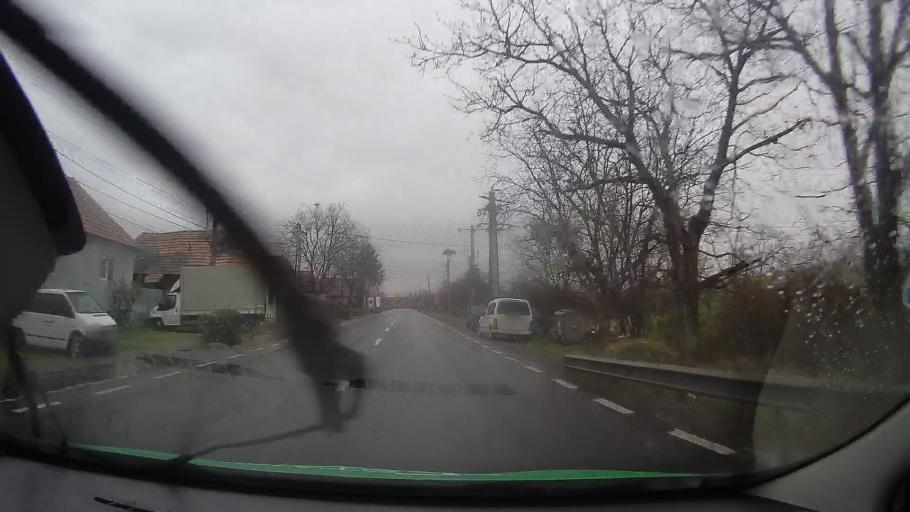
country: RO
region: Mures
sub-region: Comuna Brancovenesti
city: Valenii de Mures
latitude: 46.8874
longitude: 24.7921
